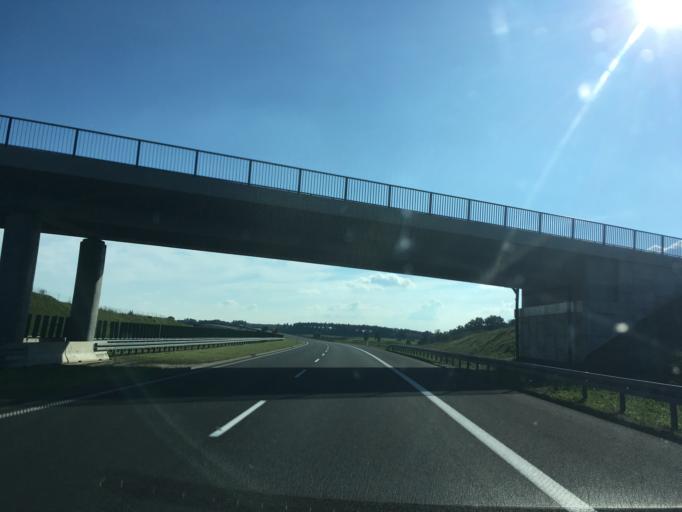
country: PL
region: Kujawsko-Pomorskie
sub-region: Powiat swiecki
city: Warlubie
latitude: 53.5782
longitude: 18.6059
